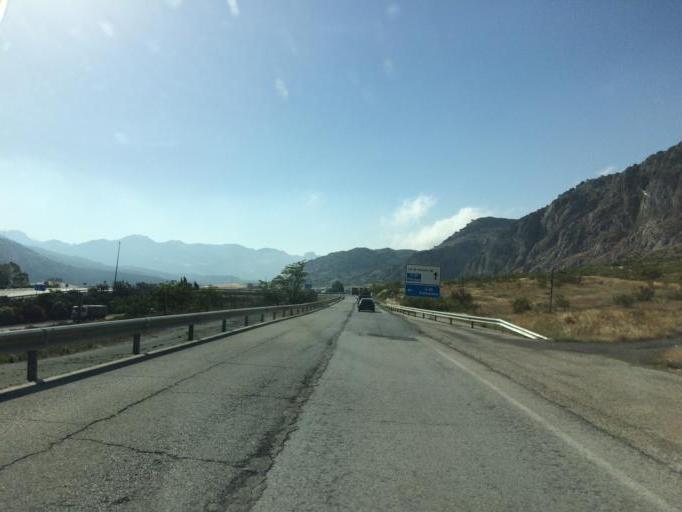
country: ES
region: Andalusia
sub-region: Provincia de Malaga
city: Casabermeja
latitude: 36.9861
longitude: -4.4657
